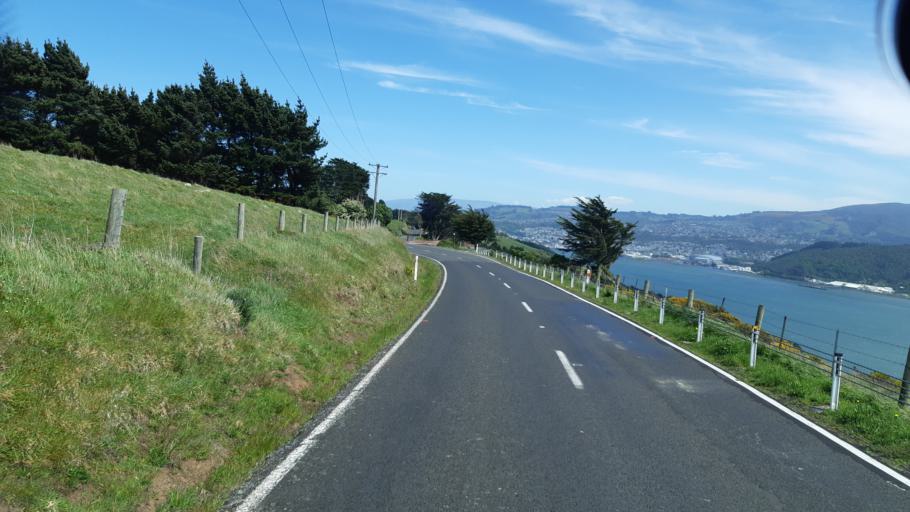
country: NZ
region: Otago
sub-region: Dunedin City
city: Portobello
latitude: -45.8848
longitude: 170.5822
